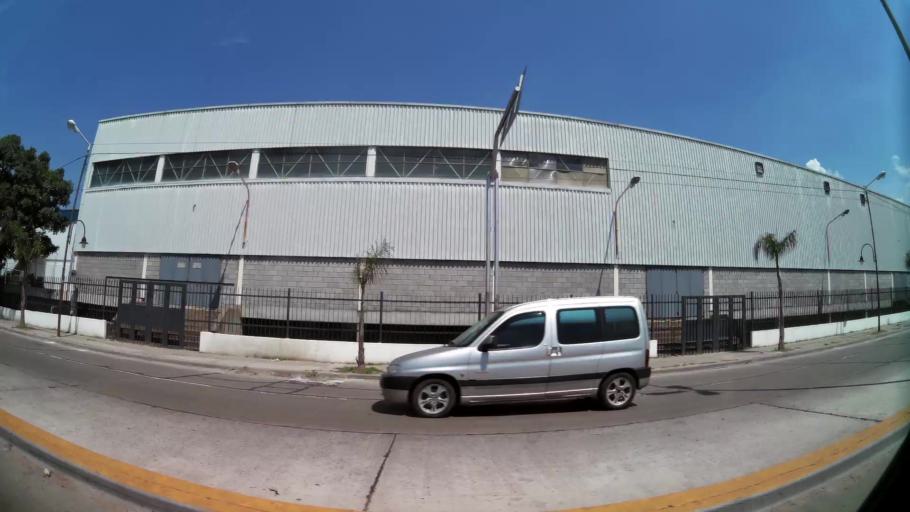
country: AR
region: Buenos Aires
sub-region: Partido de Tigre
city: Tigre
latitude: -34.4538
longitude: -58.5773
